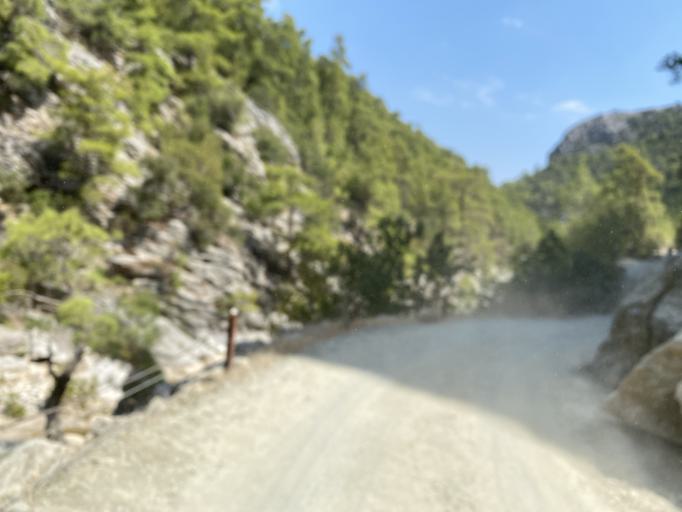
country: TR
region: Antalya
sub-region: Kemer
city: Goeynuek
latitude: 36.6808
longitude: 30.5220
